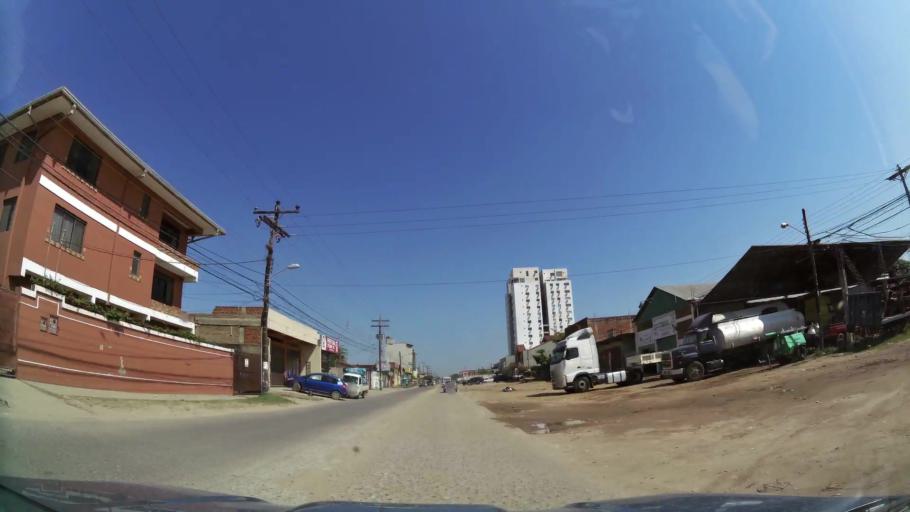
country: BO
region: Santa Cruz
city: Santa Cruz de la Sierra
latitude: -17.7379
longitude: -63.1459
